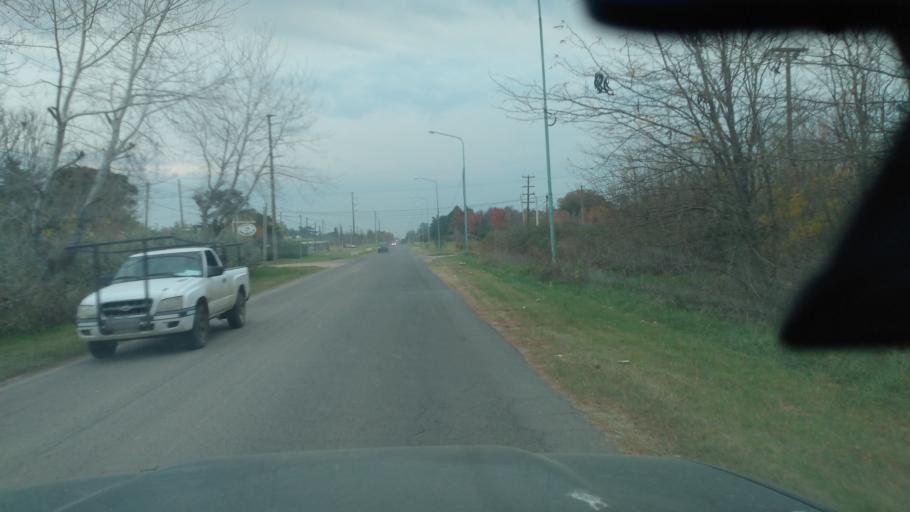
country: AR
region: Buenos Aires
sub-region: Partido de Lujan
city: Lujan
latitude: -34.5681
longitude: -59.1491
